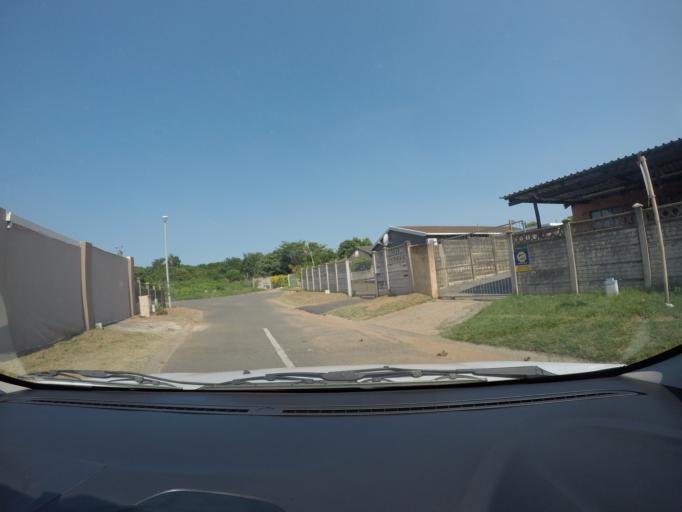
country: ZA
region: KwaZulu-Natal
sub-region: uThungulu District Municipality
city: Richards Bay
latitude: -28.7217
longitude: 32.0456
